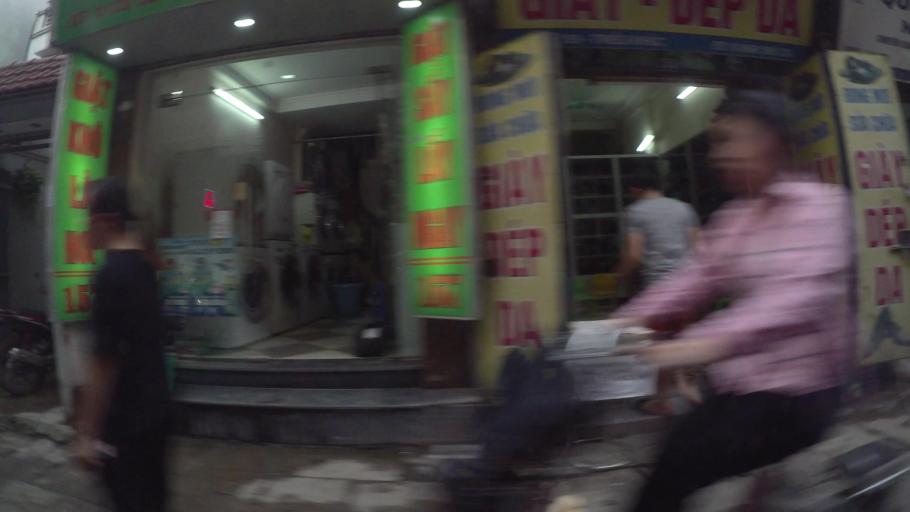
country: VN
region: Ha Noi
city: Thanh Xuan
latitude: 20.9815
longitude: 105.8007
